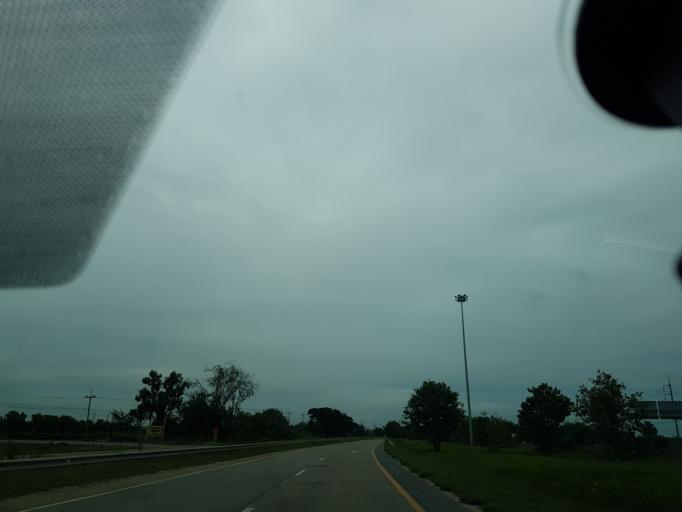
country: TH
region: Phra Nakhon Si Ayutthaya
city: Bang Pa-in
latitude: 14.1529
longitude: 100.5692
